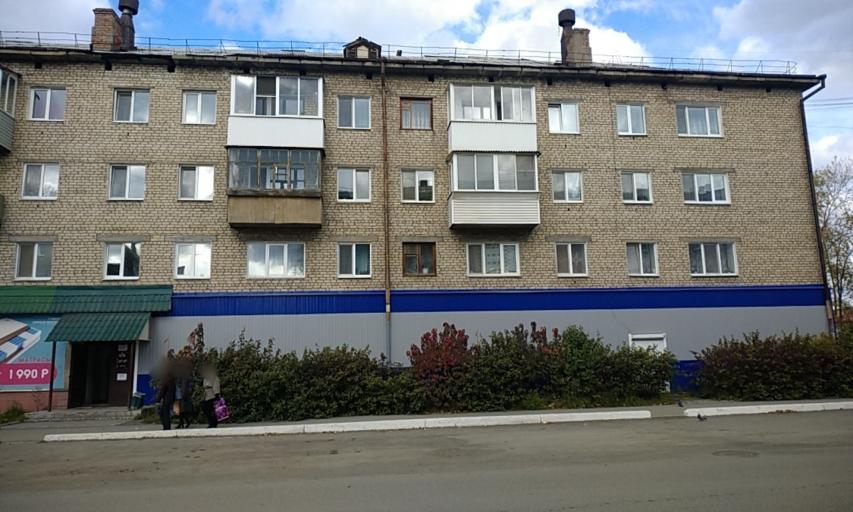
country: RU
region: Sverdlovsk
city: Krasnoural'sk
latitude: 58.3560
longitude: 60.0421
